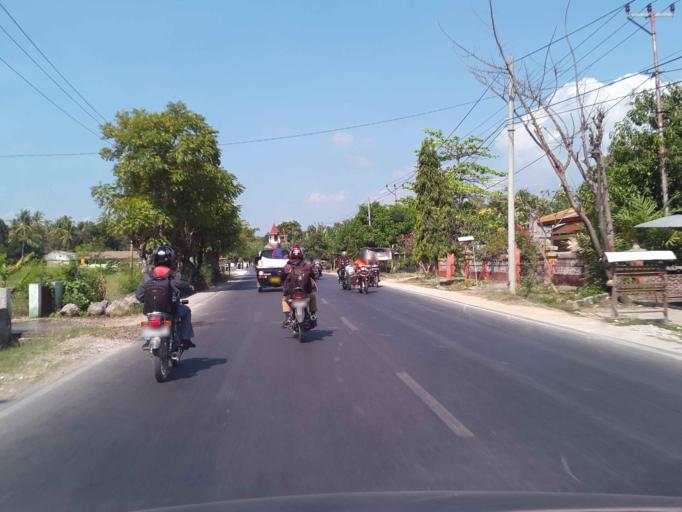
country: ID
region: East Nusa Tenggara
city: Tarus
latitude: -10.1363
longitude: 123.6802
